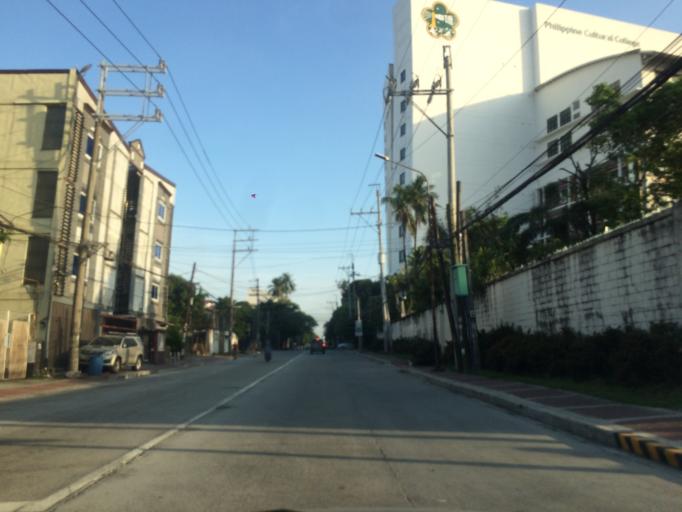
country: PH
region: Calabarzon
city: Del Monte
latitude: 14.6213
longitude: 121.0037
